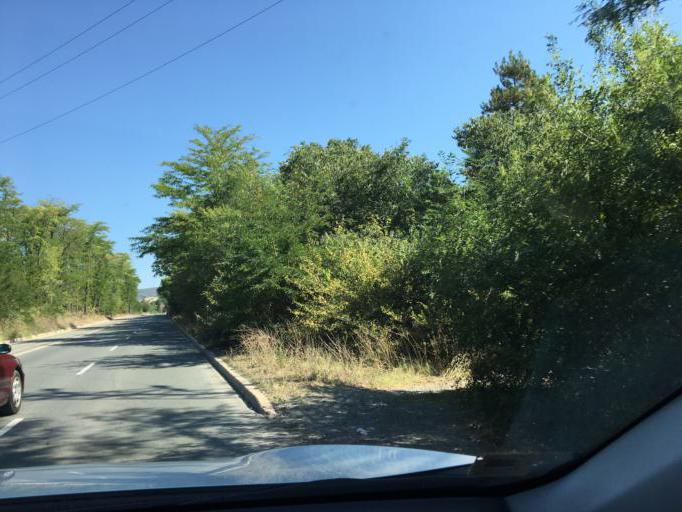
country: BG
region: Burgas
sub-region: Obshtina Kameno
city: Kameno
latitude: 42.6133
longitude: 27.3930
